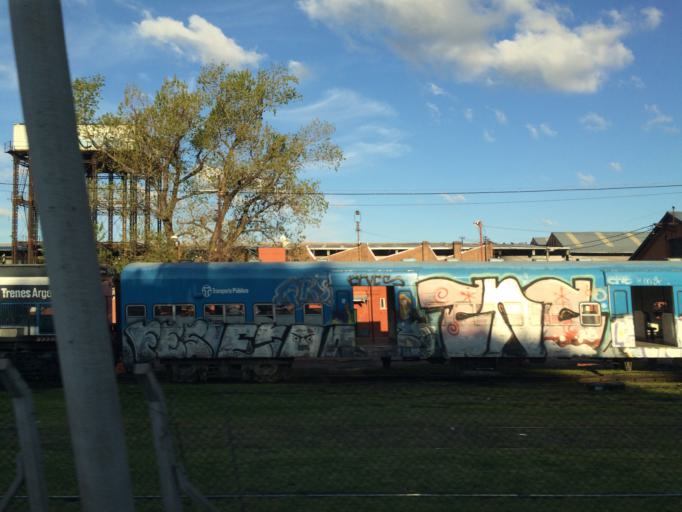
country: AR
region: Buenos Aires
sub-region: Partido de Lanus
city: Lanus
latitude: -34.7267
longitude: -58.3934
